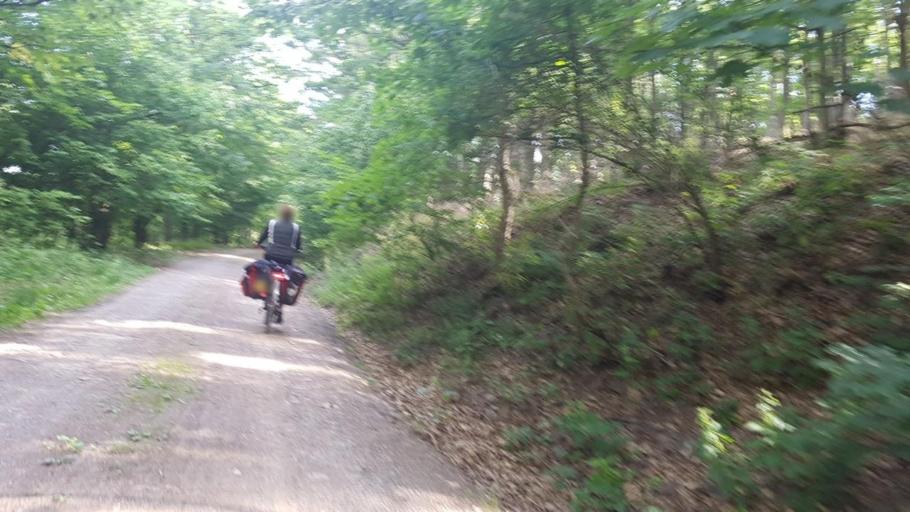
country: DE
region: North Rhine-Westphalia
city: Heimbach
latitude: 50.6204
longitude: 6.4980
